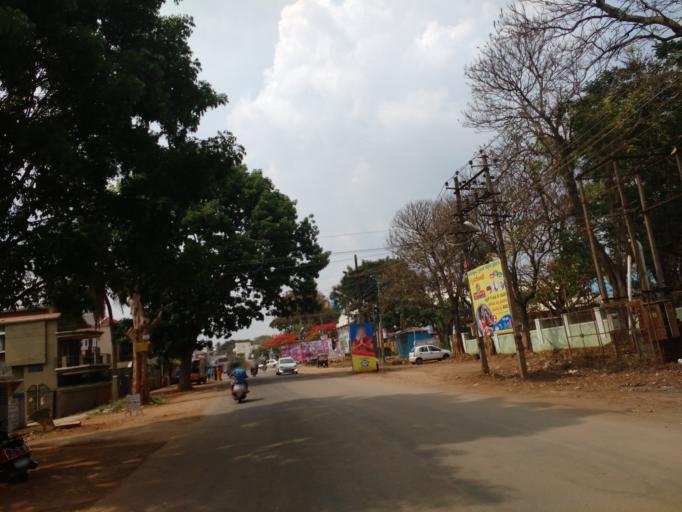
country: IN
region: Karnataka
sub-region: Hassan
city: Hassan
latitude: 13.0182
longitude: 76.1005
